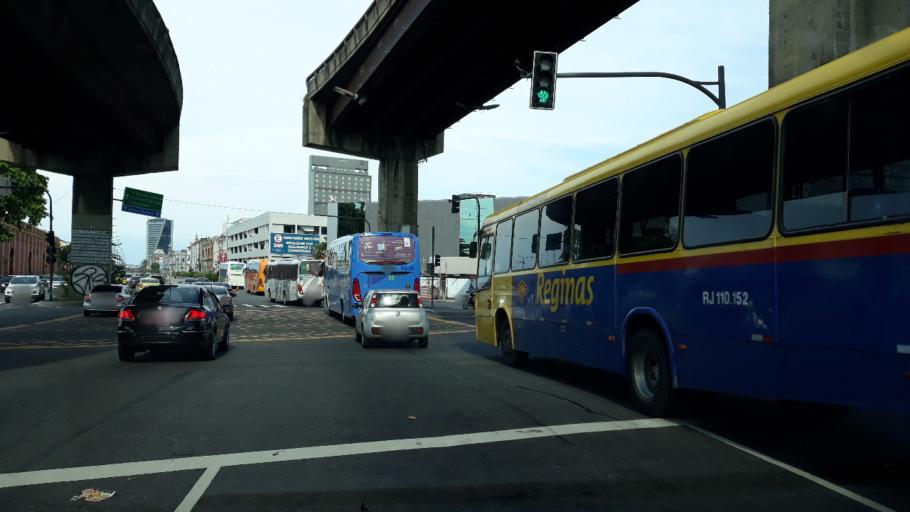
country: BR
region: Rio de Janeiro
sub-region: Rio De Janeiro
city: Rio de Janeiro
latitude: -22.8987
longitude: -43.2101
